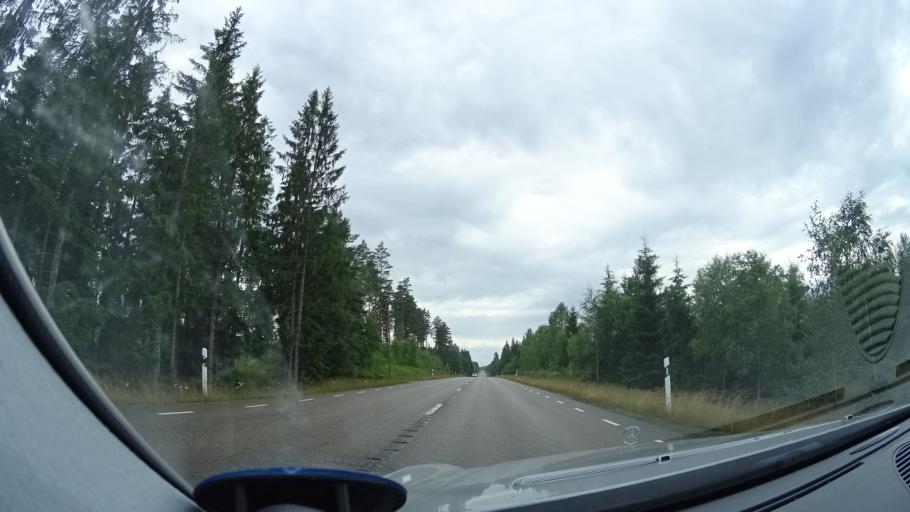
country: SE
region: Kronoberg
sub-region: Tingsryds Kommun
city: Tingsryd
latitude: 56.4569
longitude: 14.9984
